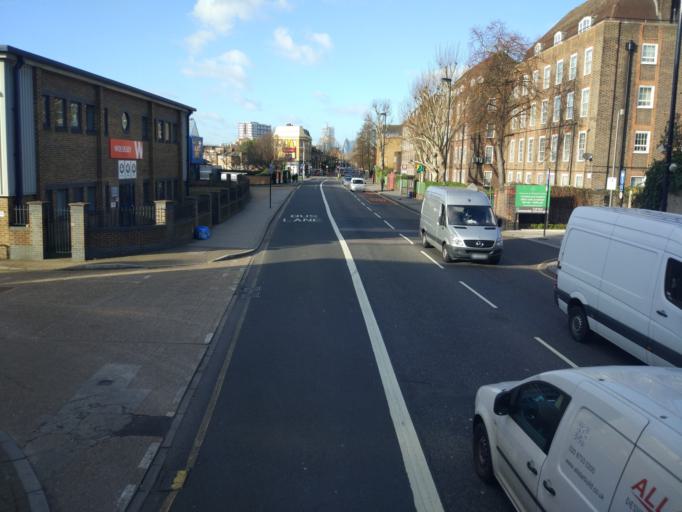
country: GB
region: England
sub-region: Greater London
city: Poplar
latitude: 51.4891
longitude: -0.0406
